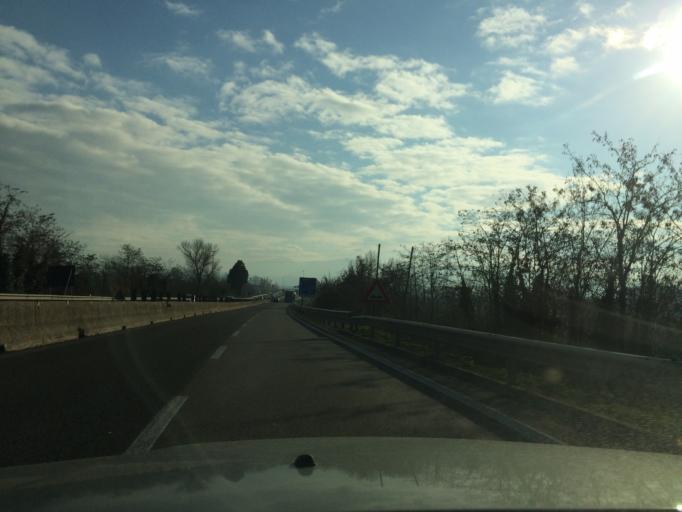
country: IT
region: Umbria
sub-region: Provincia di Terni
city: San Gemini
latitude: 42.5802
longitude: 12.5728
